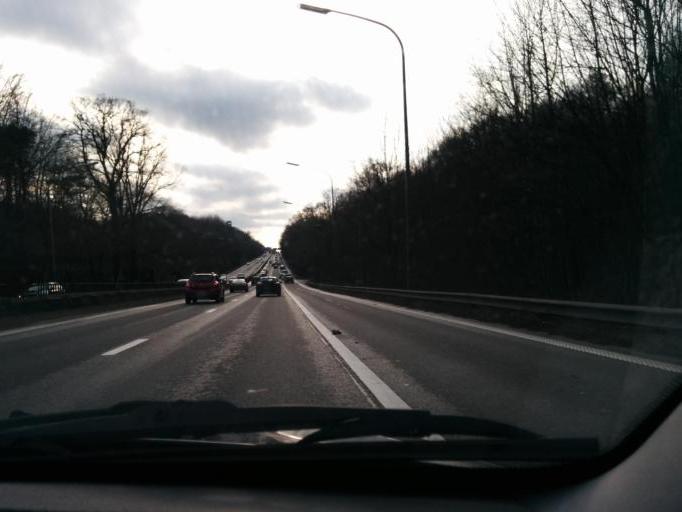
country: BE
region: Flanders
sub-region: Provincie Vlaams-Brabant
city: Wezembeek-Oppem
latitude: 50.8115
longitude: 4.4716
